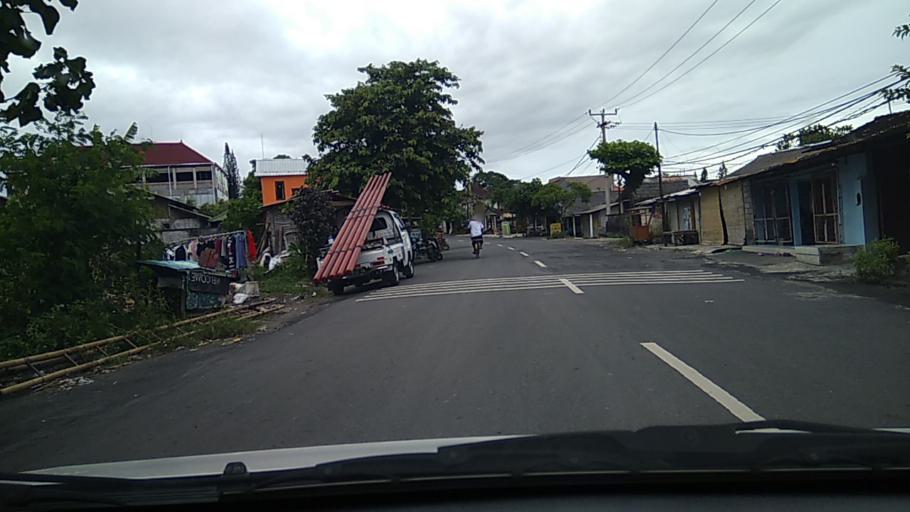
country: ID
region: Bali
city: Banjar Kertajiwa
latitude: -8.6575
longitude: 115.2634
